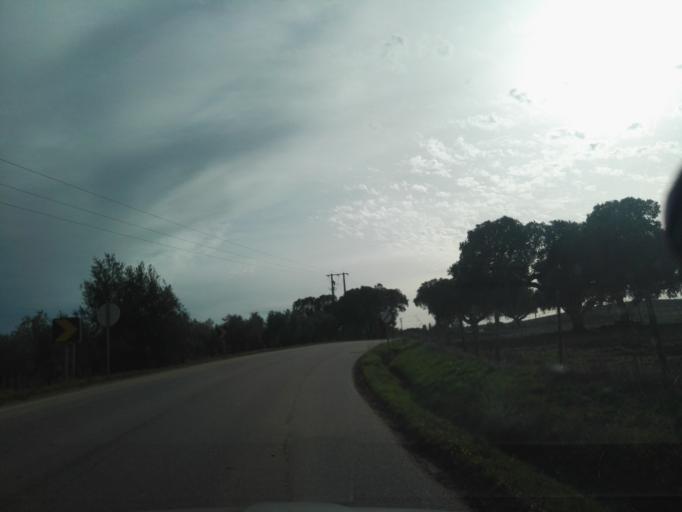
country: PT
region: Portalegre
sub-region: Elvas
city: Elvas
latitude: 38.9232
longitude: -7.1812
